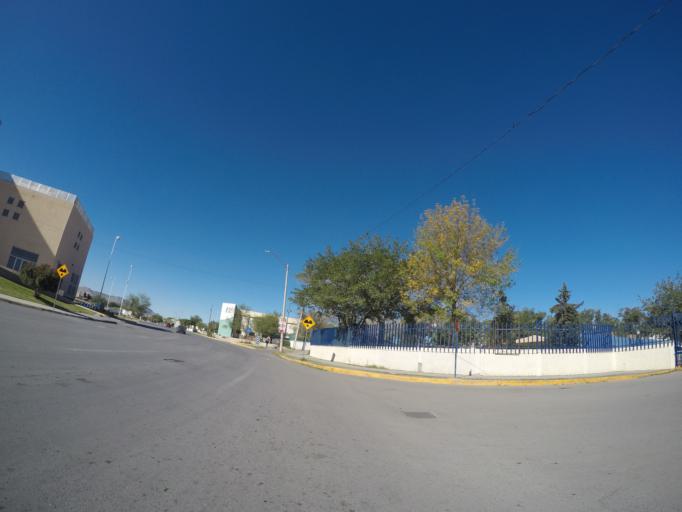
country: MX
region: Chihuahua
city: Ciudad Juarez
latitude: 31.7447
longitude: -106.4447
